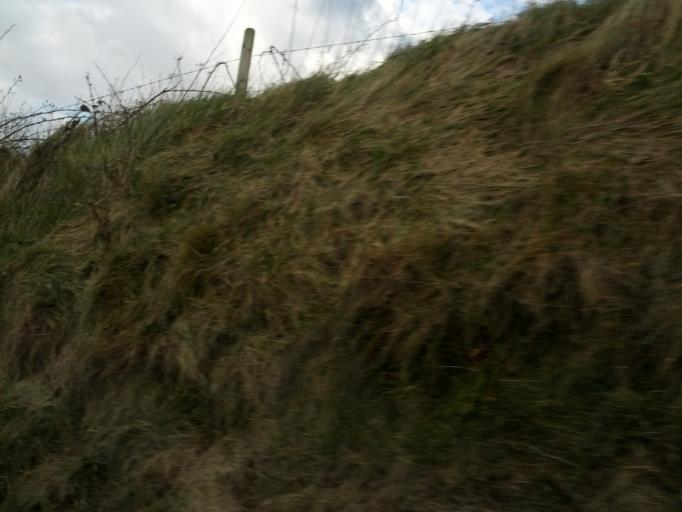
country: IE
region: Connaught
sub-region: County Galway
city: Athenry
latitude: 53.4668
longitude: -8.6526
